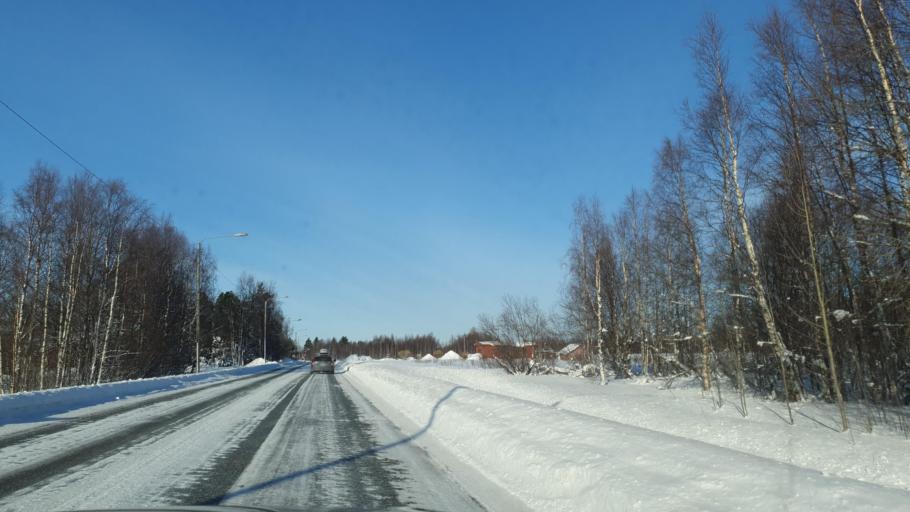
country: FI
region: Lapland
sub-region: Kemi-Tornio
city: Tornio
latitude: 66.0627
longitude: 23.9945
